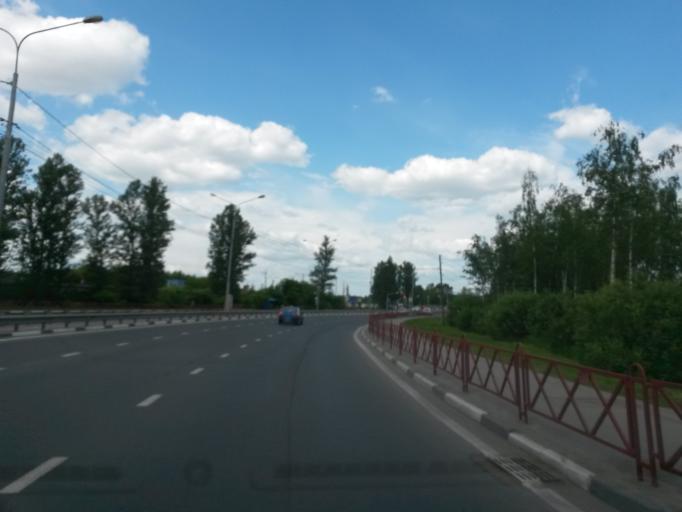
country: RU
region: Jaroslavl
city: Yaroslavl
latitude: 57.5935
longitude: 39.8938
